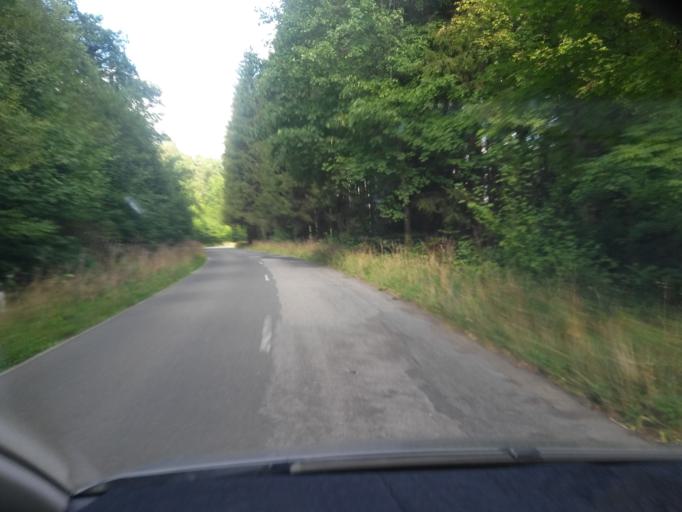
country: BE
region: Wallonia
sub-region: Province du Luxembourg
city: Libin
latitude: 50.0268
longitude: 5.3049
